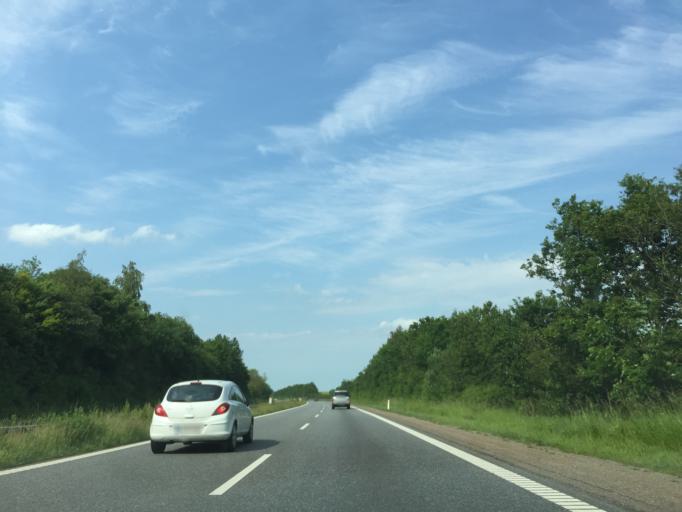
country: DK
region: Central Jutland
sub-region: Arhus Kommune
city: Logten
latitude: 56.2642
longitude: 10.3269
